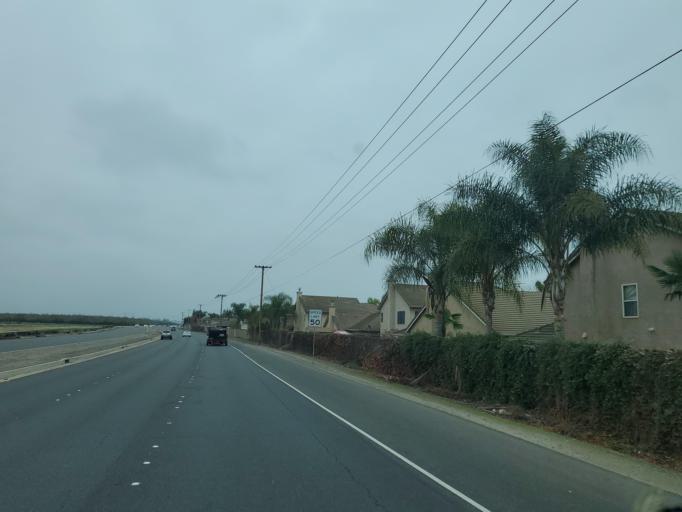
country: US
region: California
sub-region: Stanislaus County
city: Del Rio
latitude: 37.7002
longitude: -121.0207
